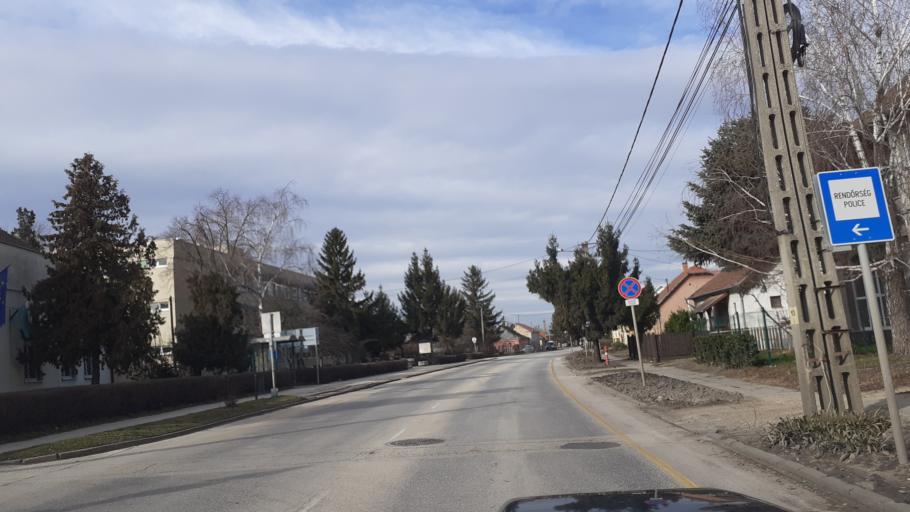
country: HU
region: Fejer
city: Sarbogard
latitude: 46.8884
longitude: 18.6187
